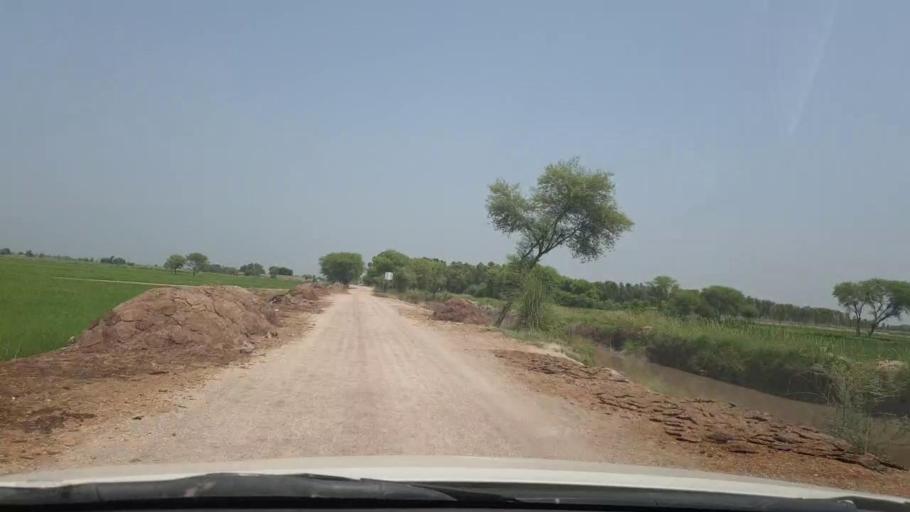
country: PK
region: Sindh
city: Rustam jo Goth
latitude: 28.0288
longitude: 68.7770
